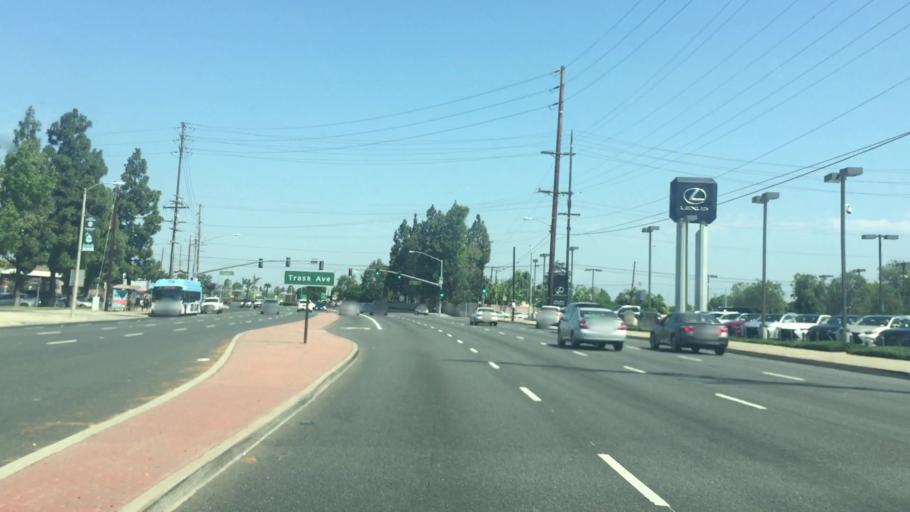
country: US
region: California
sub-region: Orange County
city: Westminster
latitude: 33.7654
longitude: -117.9897
